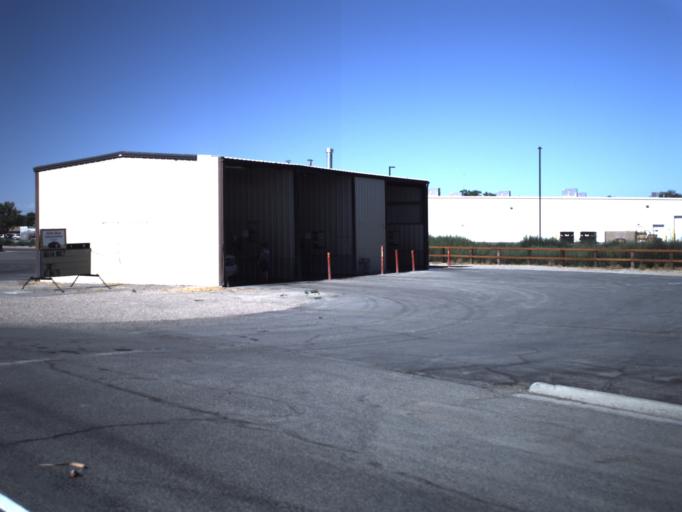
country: US
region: Utah
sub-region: Millard County
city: Delta
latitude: 39.3543
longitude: -112.5633
